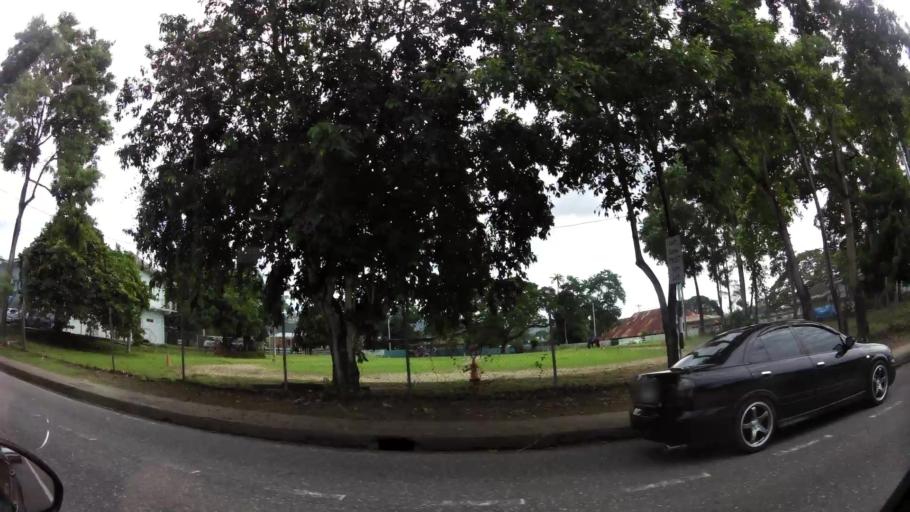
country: TT
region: City of Port of Spain
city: Port-of-Spain
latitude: 10.6750
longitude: -61.5292
